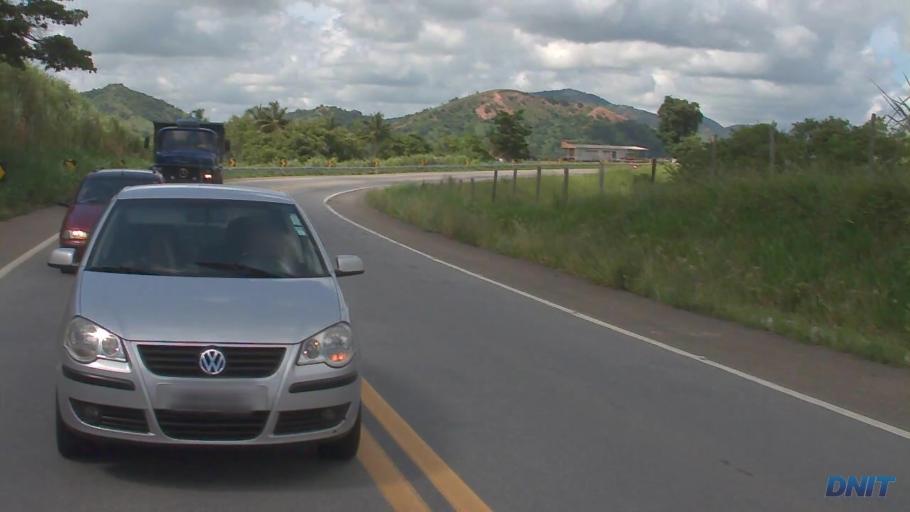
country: BR
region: Minas Gerais
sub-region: Belo Oriente
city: Belo Oriente
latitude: -19.1367
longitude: -42.2150
